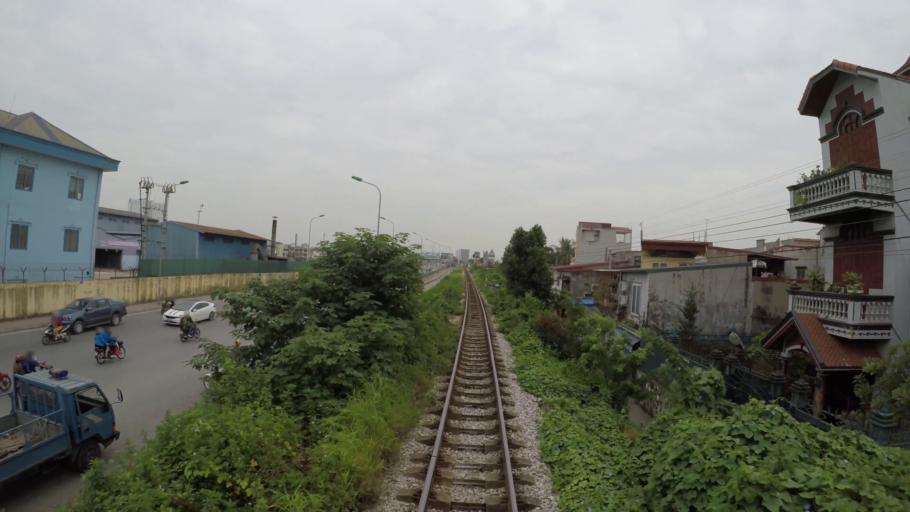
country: VN
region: Hai Phong
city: An Duong
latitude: 20.8722
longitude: 106.6479
